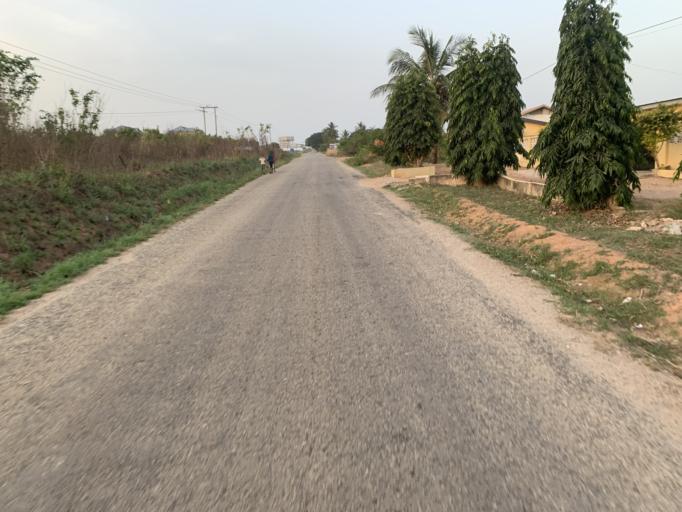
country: GH
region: Central
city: Winneba
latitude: 5.3629
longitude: -0.6213
